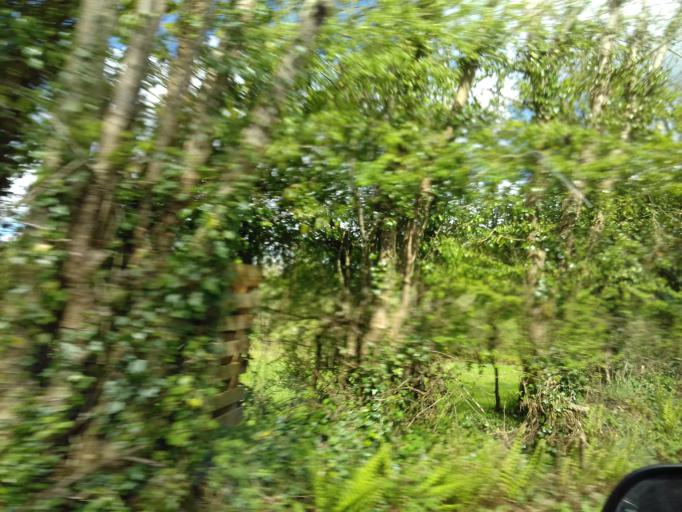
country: IE
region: Leinster
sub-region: Loch Garman
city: Castlebridge
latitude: 52.3766
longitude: -6.5038
